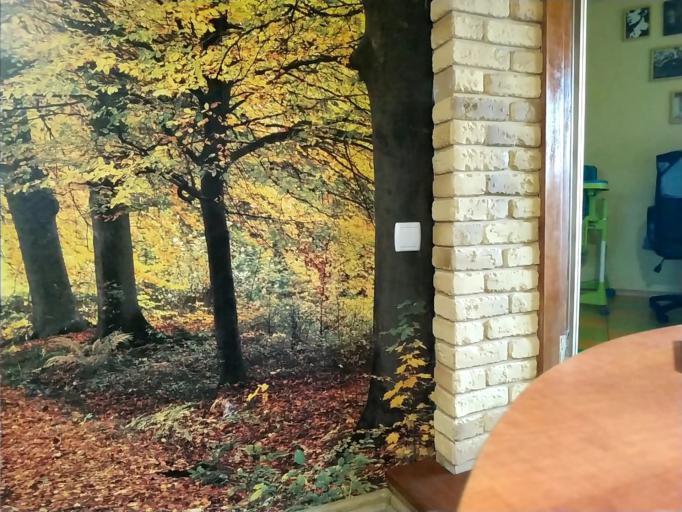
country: RU
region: Leningrad
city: Tolmachevo
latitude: 58.9445
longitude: 29.6576
